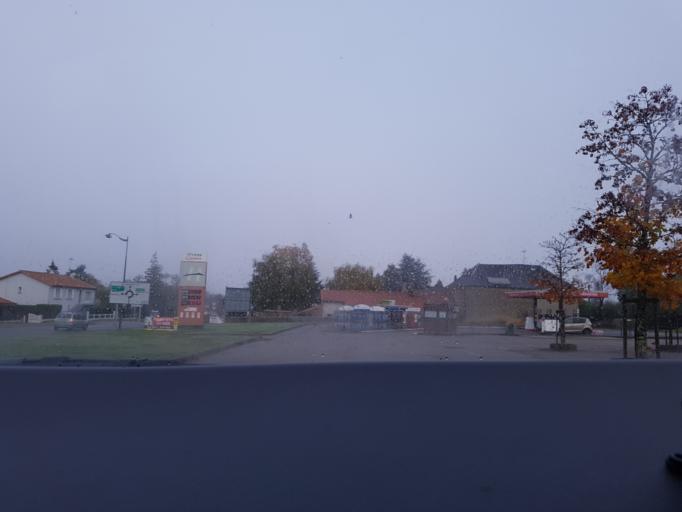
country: FR
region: Poitou-Charentes
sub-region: Departement des Deux-Sevres
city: Parthenay
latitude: 46.6351
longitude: -0.2449
